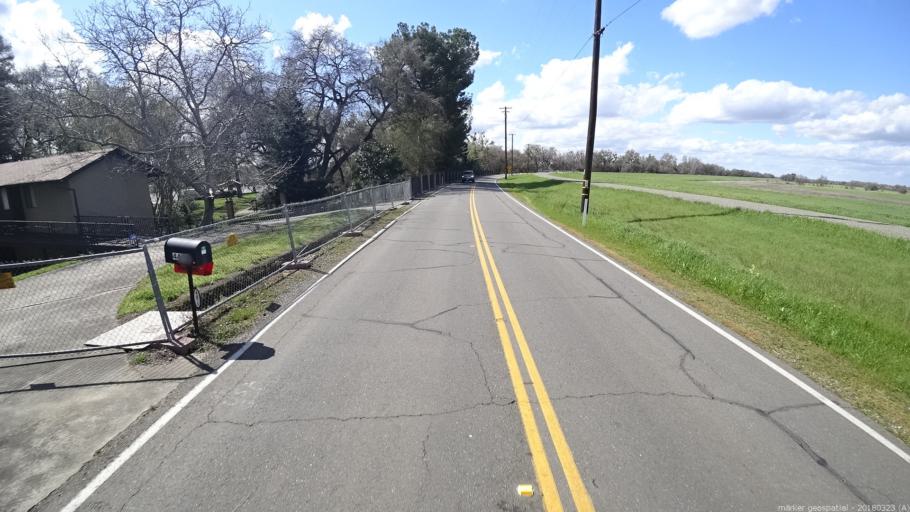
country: US
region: California
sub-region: Yolo County
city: West Sacramento
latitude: 38.6441
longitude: -121.5903
